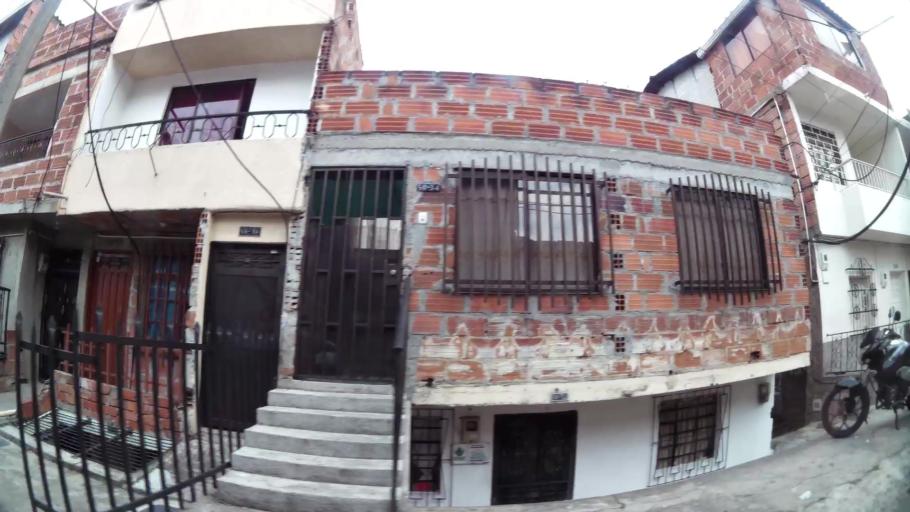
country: CO
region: Antioquia
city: Medellin
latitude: 6.2899
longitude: -75.5579
